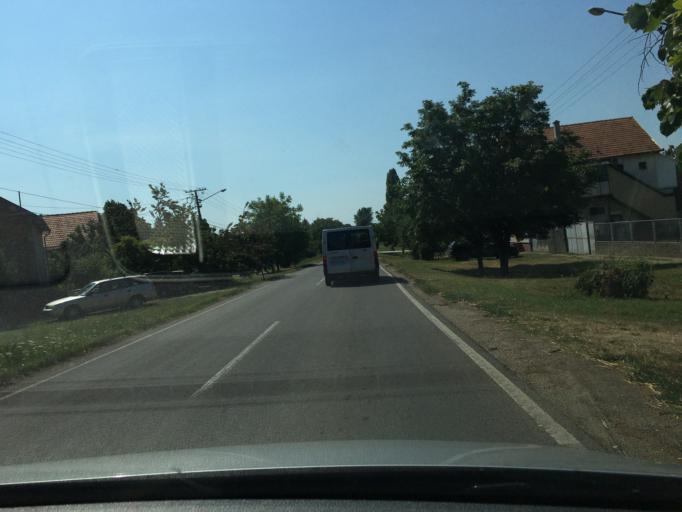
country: RS
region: Central Serbia
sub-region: Belgrade
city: Grocka
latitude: 44.7637
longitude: 20.7332
